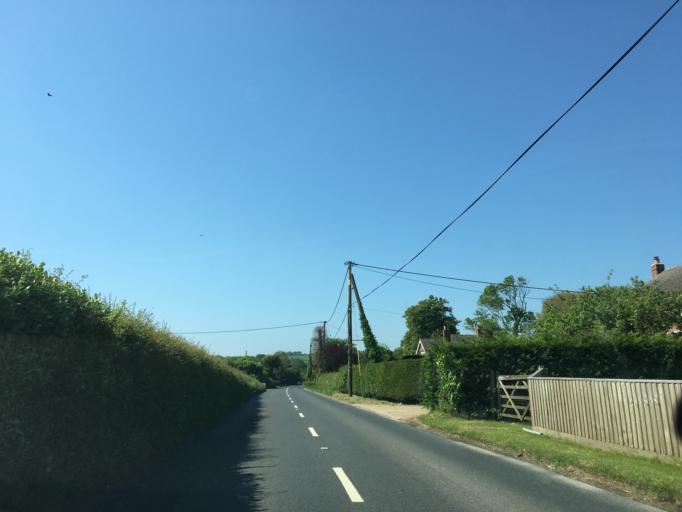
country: GB
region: England
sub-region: Isle of Wight
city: Ryde
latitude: 50.6996
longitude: -1.1705
